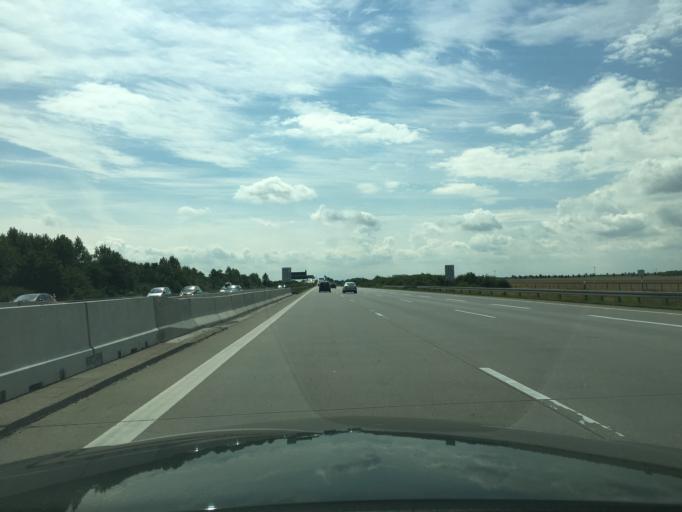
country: DE
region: Saxony
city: Schkeuditz
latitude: 51.4186
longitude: 12.1929
